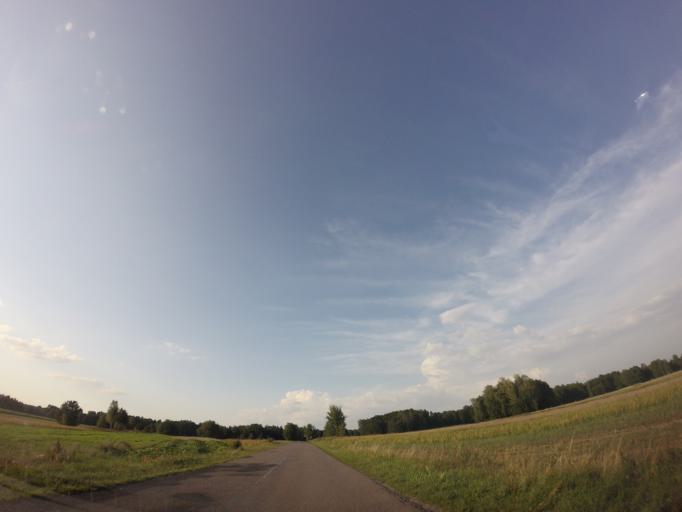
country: PL
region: Lublin Voivodeship
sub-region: Powiat pulawski
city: Kurow
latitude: 51.4199
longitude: 22.2023
